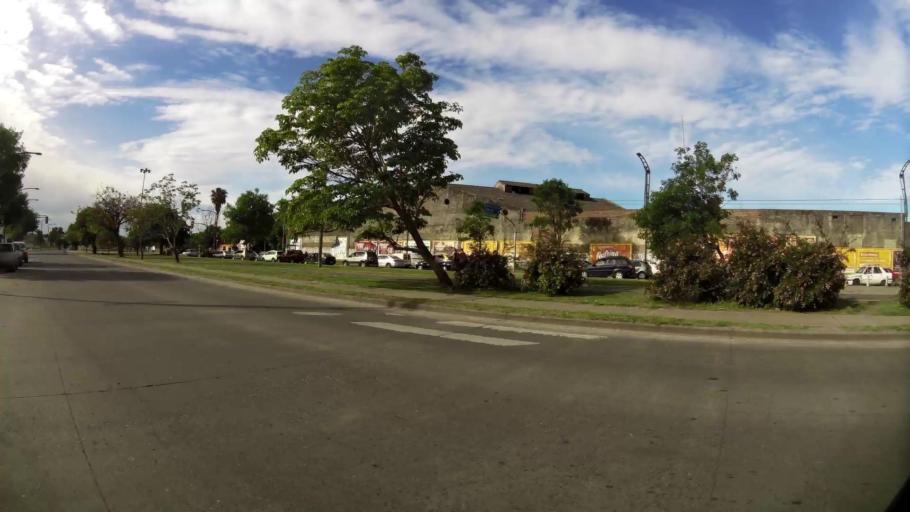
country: AR
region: Santa Fe
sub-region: Departamento de Rosario
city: Rosario
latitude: -32.9205
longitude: -60.6885
